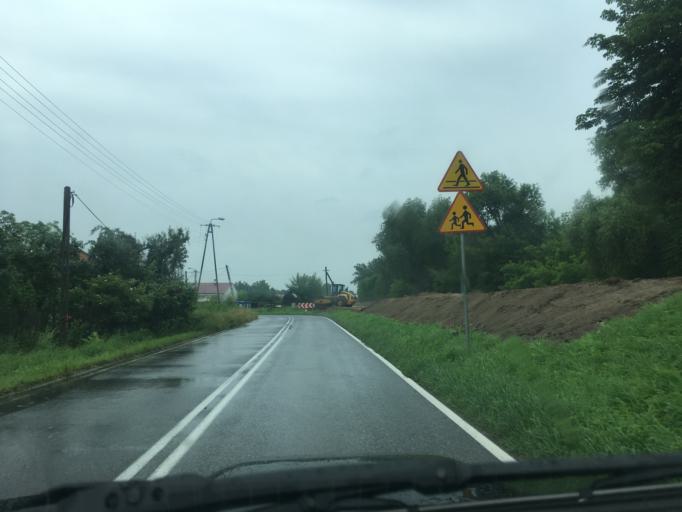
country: PL
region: Masovian Voivodeship
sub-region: Powiat piaseczynski
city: Gora Kalwaria
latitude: 51.9816
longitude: 21.2616
